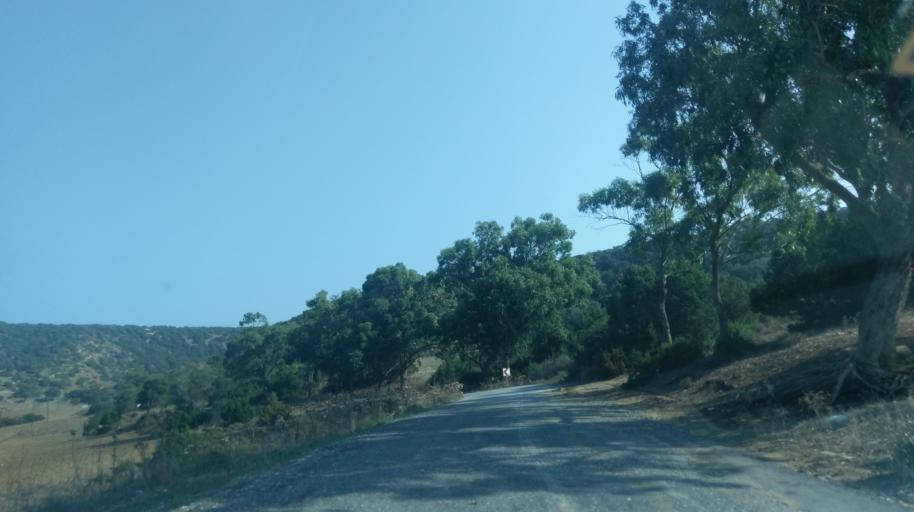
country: CY
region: Ammochostos
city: Rizokarpaso
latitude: 35.6481
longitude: 34.5473
